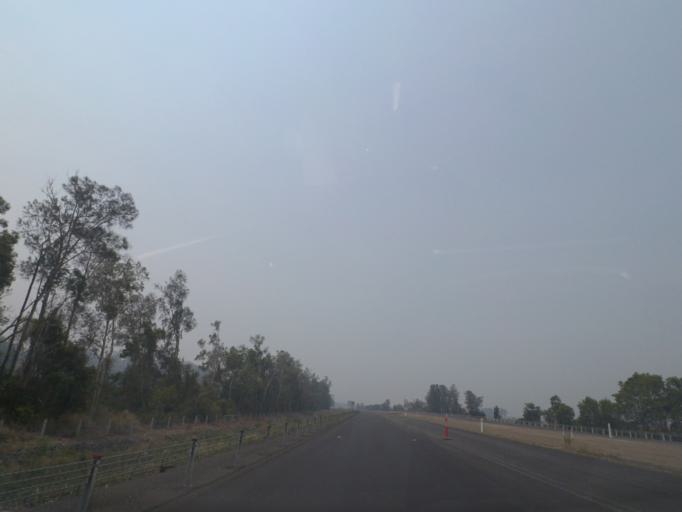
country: AU
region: New South Wales
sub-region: Ballina
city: Ballina
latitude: -28.8795
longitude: 153.4868
